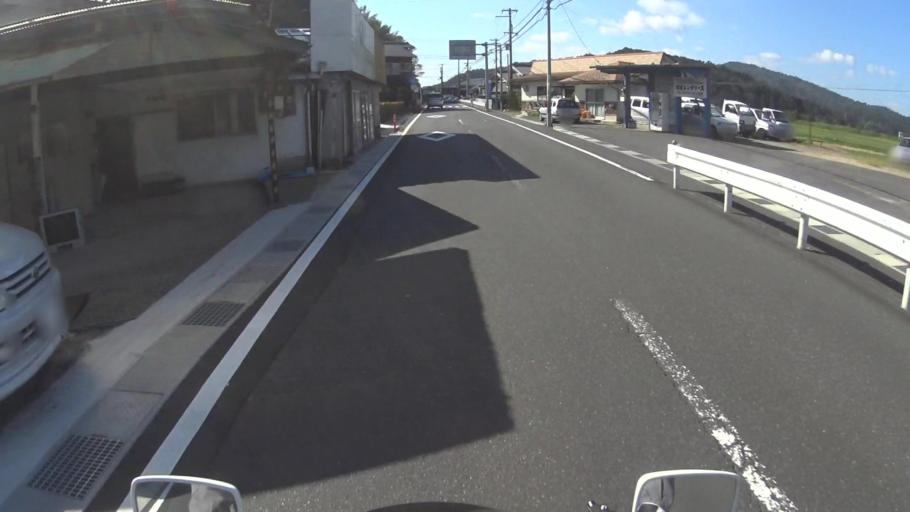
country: JP
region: Kyoto
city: Miyazu
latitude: 35.7111
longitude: 135.1064
